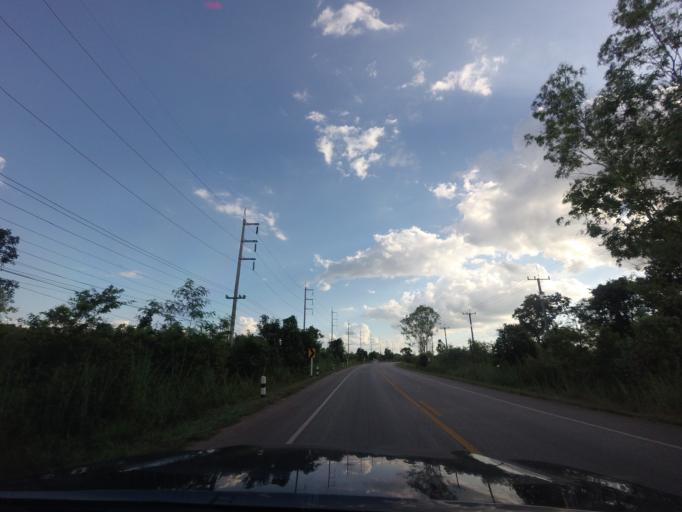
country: TH
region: Changwat Udon Thani
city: Thung Fon
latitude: 17.4699
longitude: 103.1932
